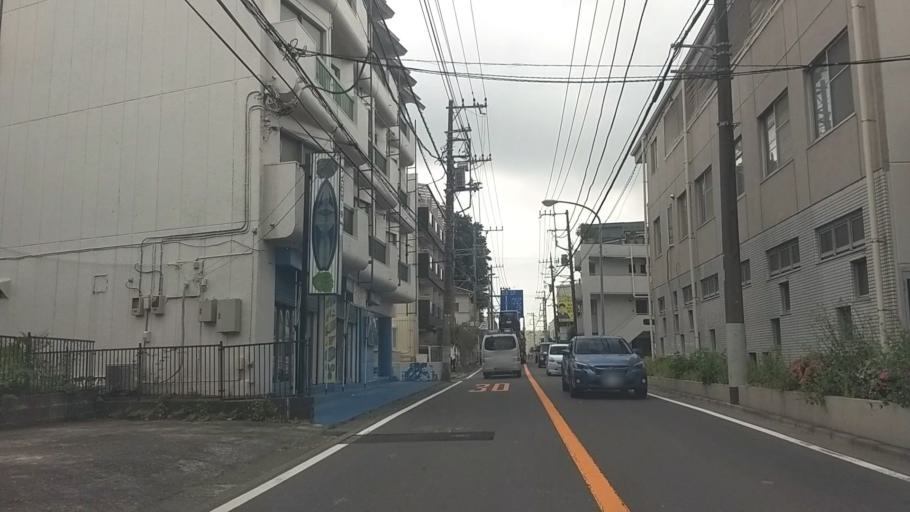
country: JP
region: Kanagawa
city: Kamakura
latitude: 35.3836
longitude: 139.5364
